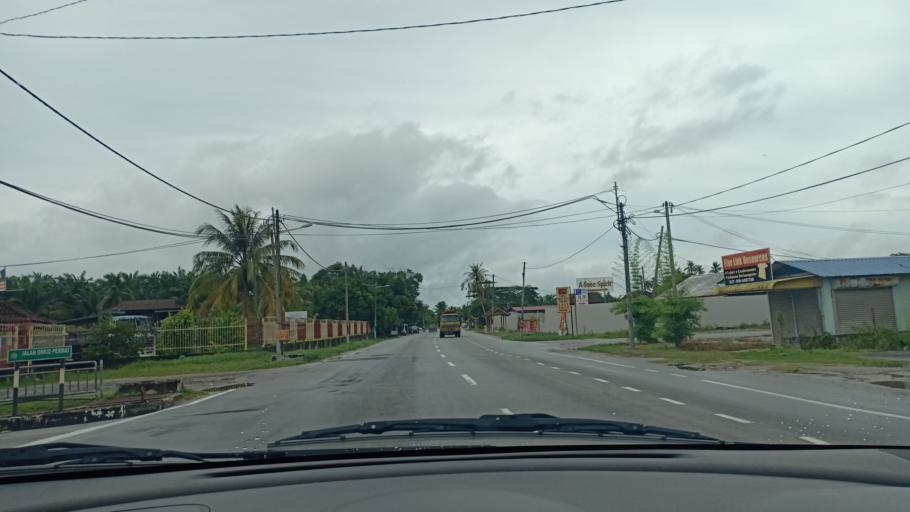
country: MY
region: Penang
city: Kepala Batas
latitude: 5.4949
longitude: 100.4475
